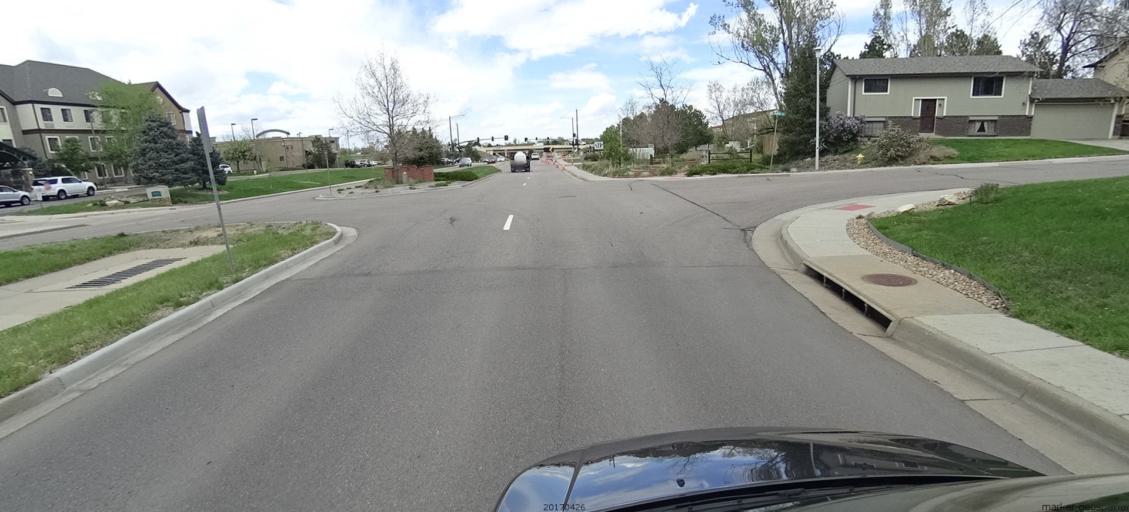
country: US
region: Colorado
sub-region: Douglas County
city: Acres Green
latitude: 39.5614
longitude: -104.8966
